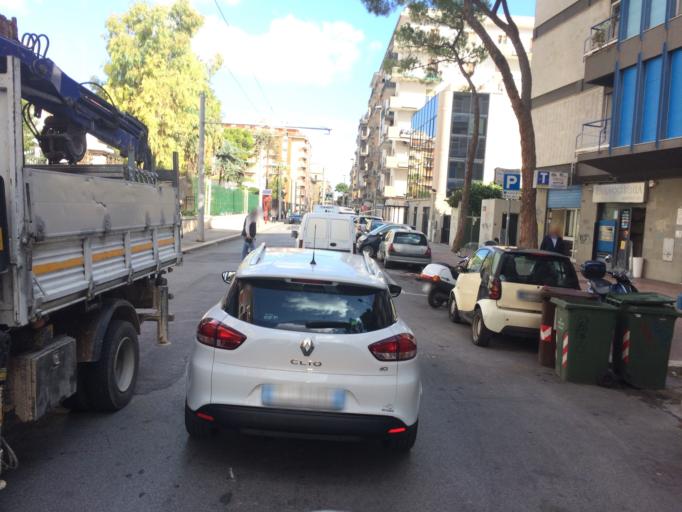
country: IT
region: Apulia
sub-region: Provincia di Bari
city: Bari
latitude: 41.1053
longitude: 16.8717
